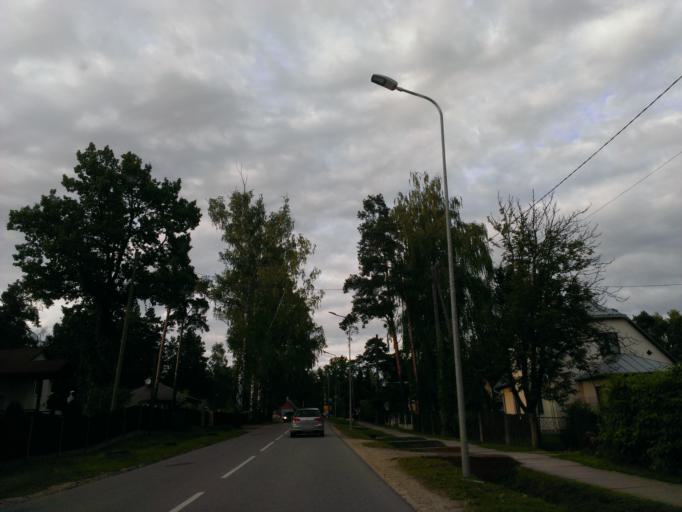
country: LV
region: Ogre
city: Ogre
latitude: 56.8203
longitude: 24.5812
